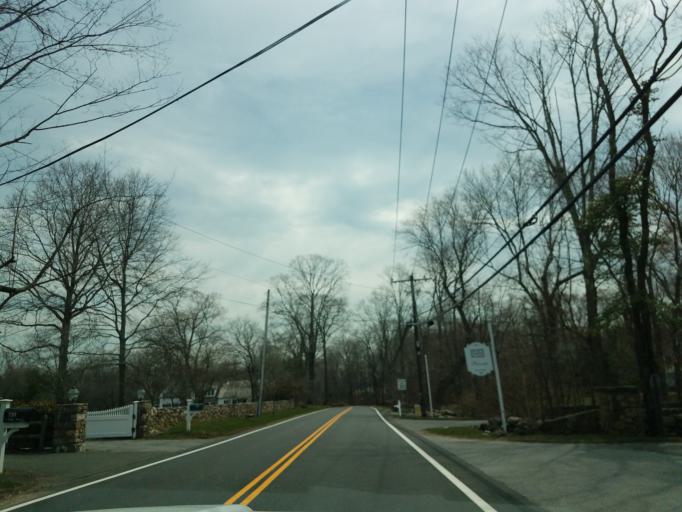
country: US
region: Connecticut
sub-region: Fairfield County
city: Glenville
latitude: 41.0841
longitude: -73.6465
